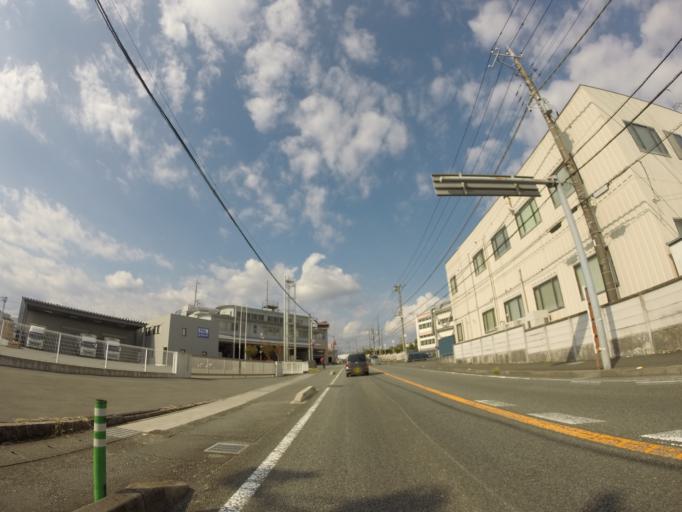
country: JP
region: Shizuoka
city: Fujinomiya
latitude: 35.2197
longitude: 138.6215
